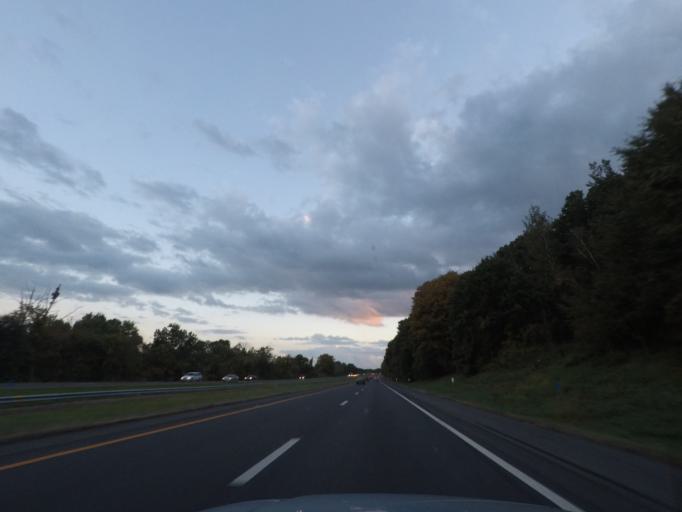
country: US
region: New York
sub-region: Ulster County
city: Lake Katrine
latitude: 41.9957
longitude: -74.0050
